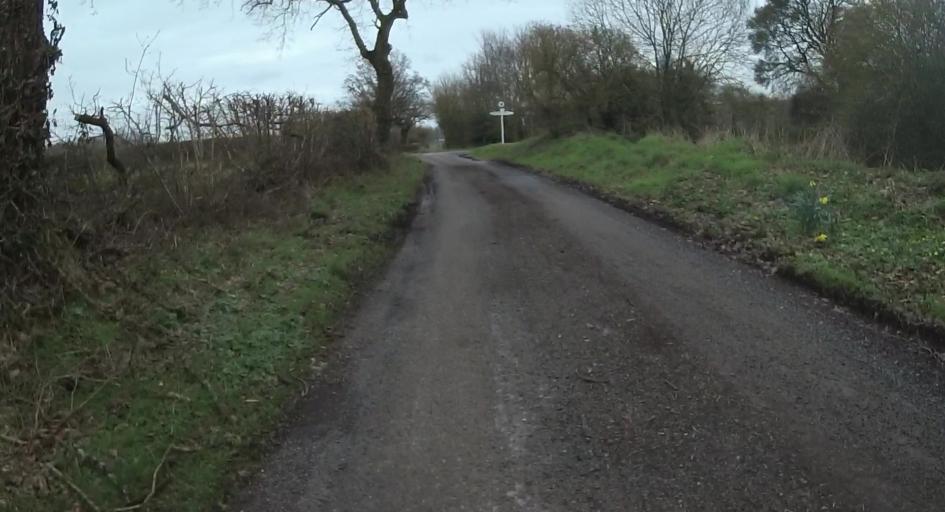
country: GB
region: England
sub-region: Hampshire
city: Overton
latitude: 51.2611
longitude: -1.2402
